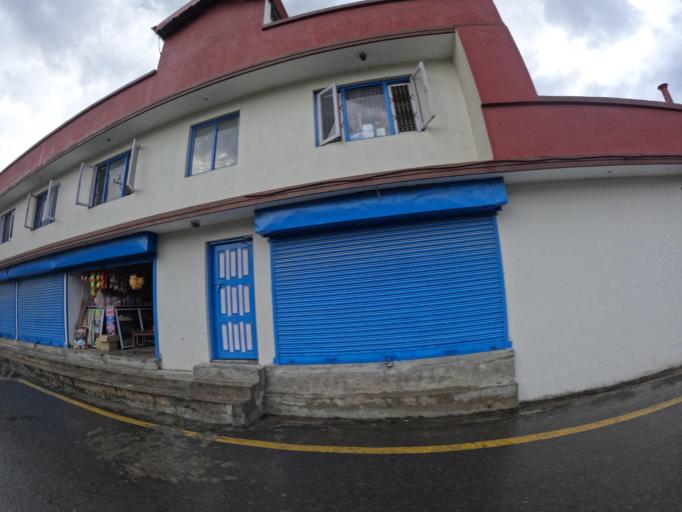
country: NP
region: Central Region
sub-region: Bagmati Zone
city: Kathmandu
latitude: 27.7741
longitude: 85.3372
